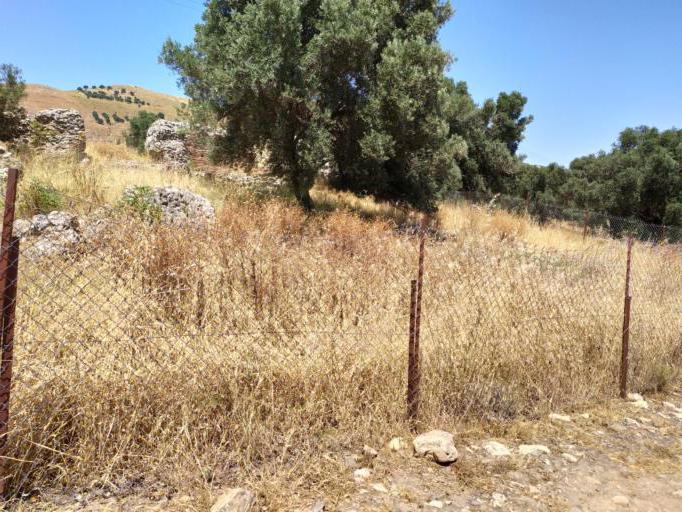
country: GR
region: Crete
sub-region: Nomos Irakleiou
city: Agioi Deka
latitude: 35.0590
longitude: 24.9492
